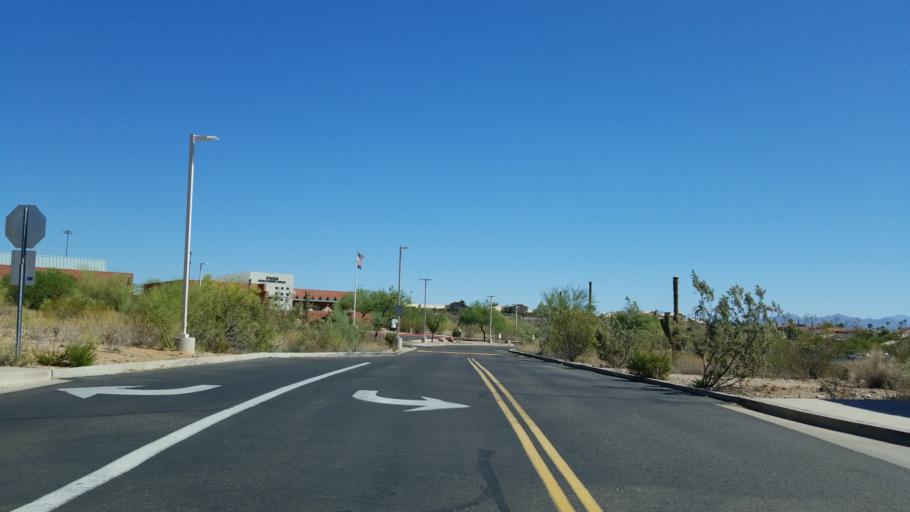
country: US
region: Arizona
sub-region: Maricopa County
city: Fountain Hills
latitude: 33.6142
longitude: -111.7336
